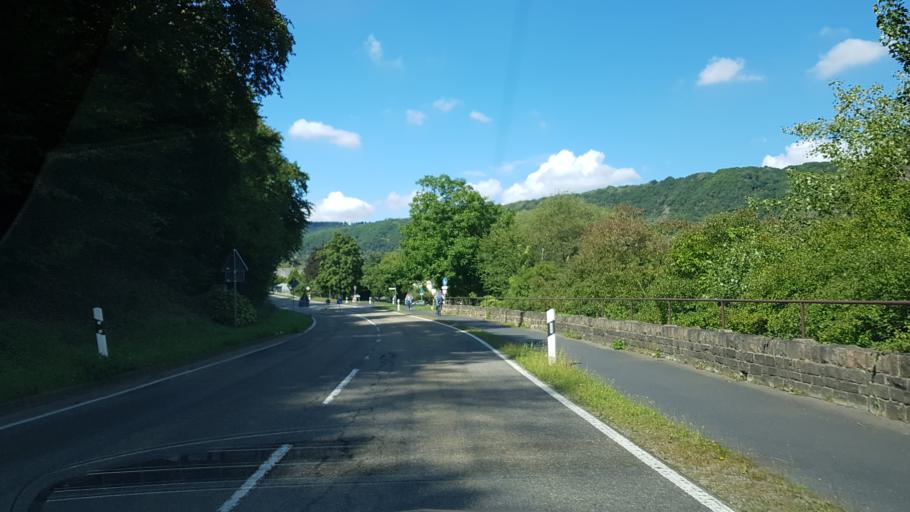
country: DE
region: Rheinland-Pfalz
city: Ellenz-Poltersdorf
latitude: 50.1067
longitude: 7.2169
